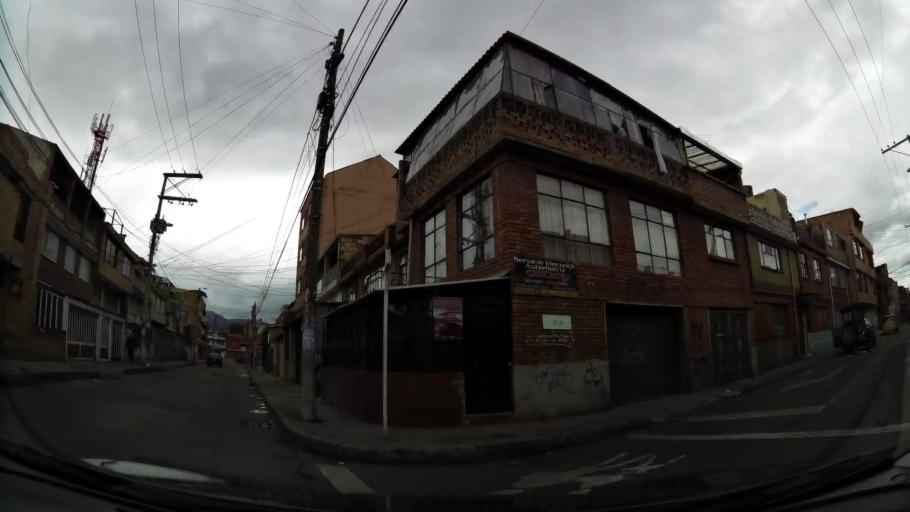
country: CO
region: Bogota D.C.
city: Bogota
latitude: 4.6818
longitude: -74.0945
